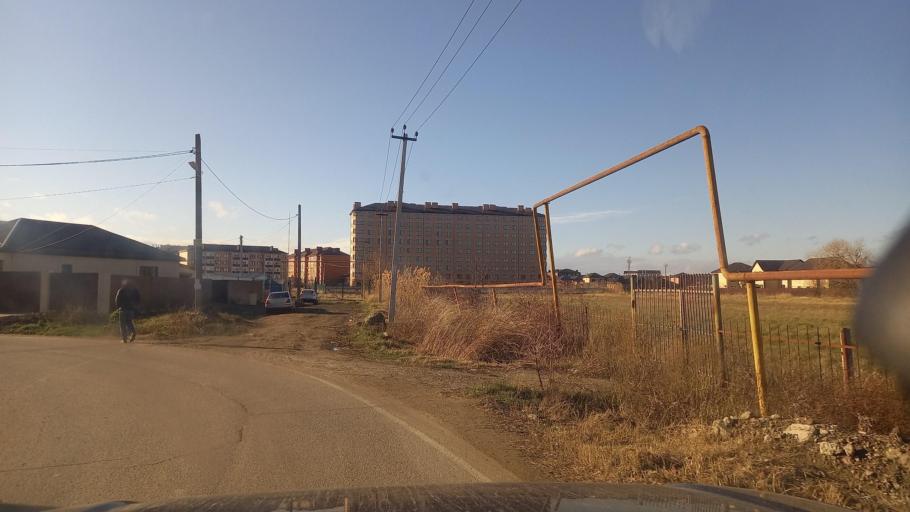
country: RU
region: Adygeya
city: Yablonovskiy
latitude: 44.9924
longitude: 38.9371
